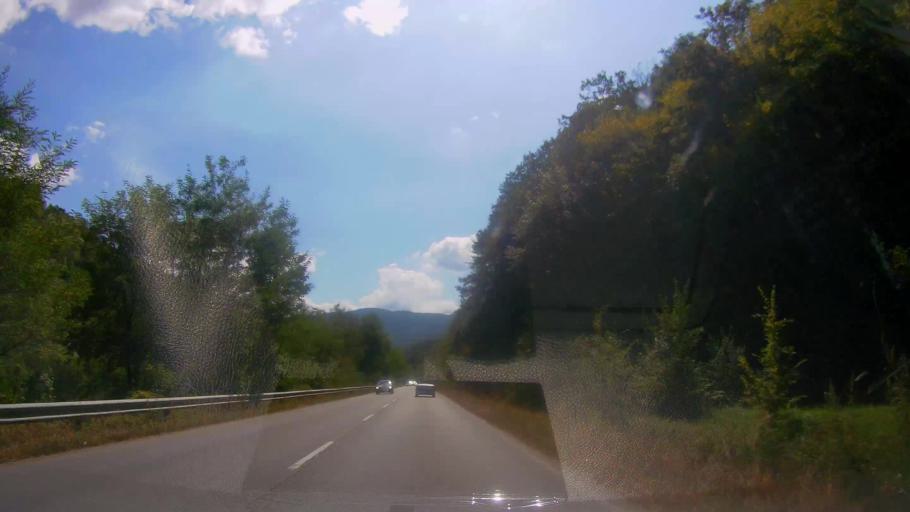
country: BG
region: Stara Zagora
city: Gurkovo
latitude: 42.7302
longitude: 25.7121
